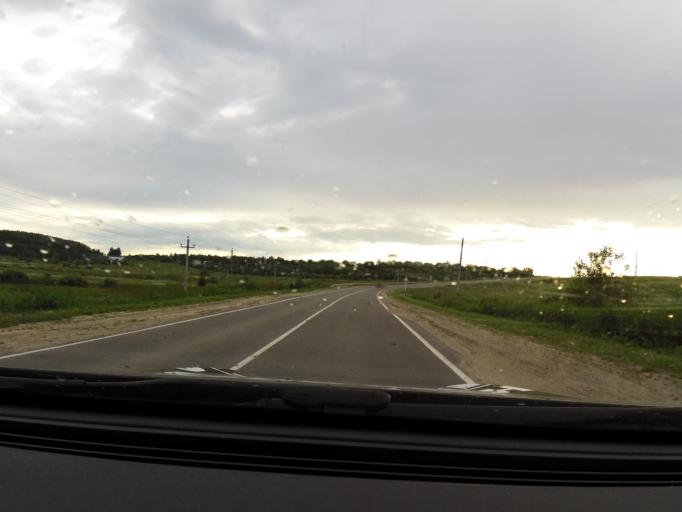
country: RU
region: Vladimir
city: Stavrovo
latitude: 56.1217
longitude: 40.0061
